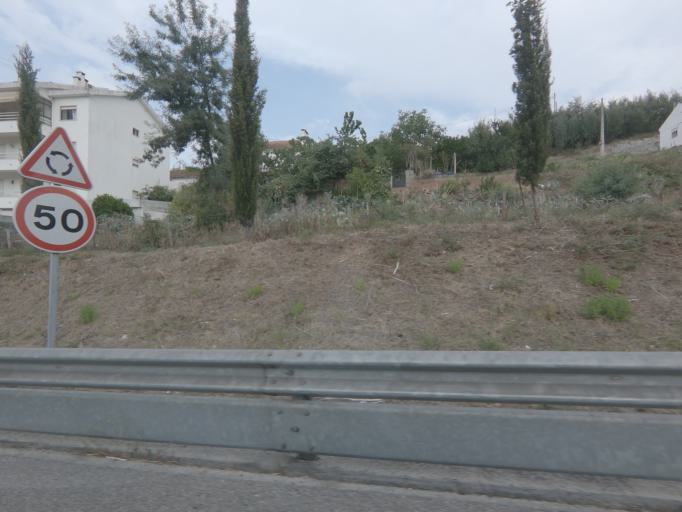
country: PT
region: Coimbra
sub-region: Coimbra
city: Coimbra
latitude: 40.2121
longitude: -8.4462
